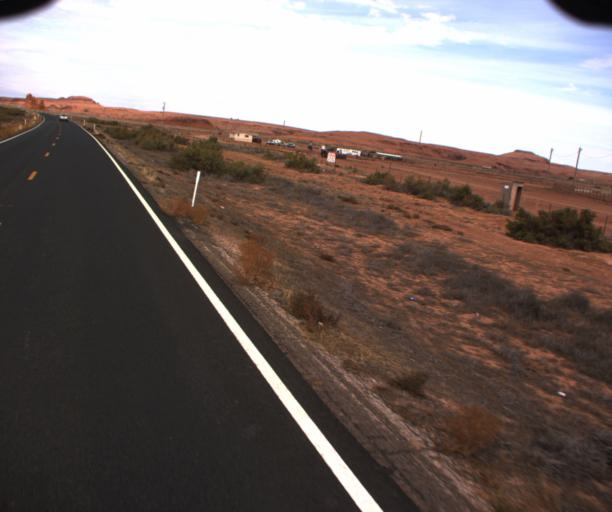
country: US
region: Arizona
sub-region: Apache County
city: Many Farms
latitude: 36.7343
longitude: -109.6334
